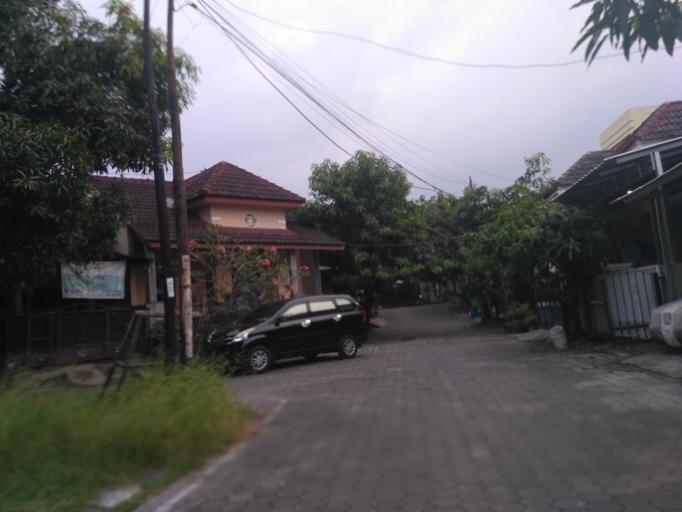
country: ID
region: Central Java
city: Mranggen
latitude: -7.0406
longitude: 110.4712
